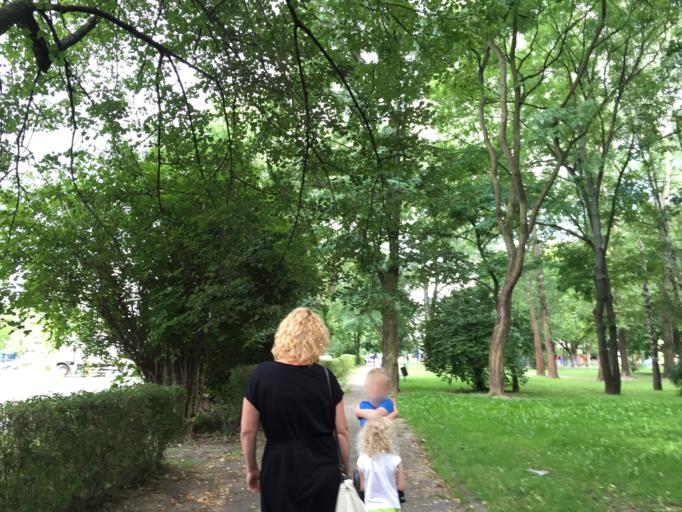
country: PL
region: Lesser Poland Voivodeship
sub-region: Powiat wielicki
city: Kokotow
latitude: 50.0713
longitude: 20.0323
